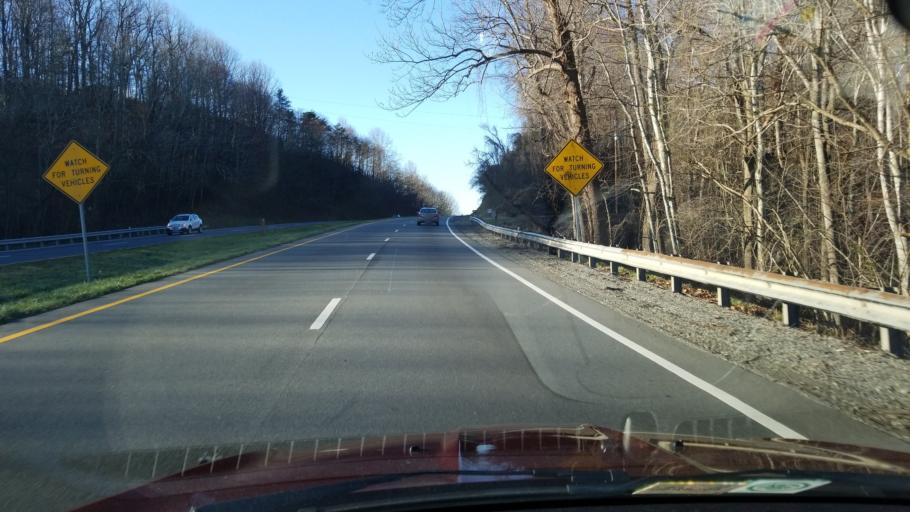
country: US
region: Virginia
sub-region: Franklin County
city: Rocky Mount
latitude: 37.0368
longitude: -79.8758
